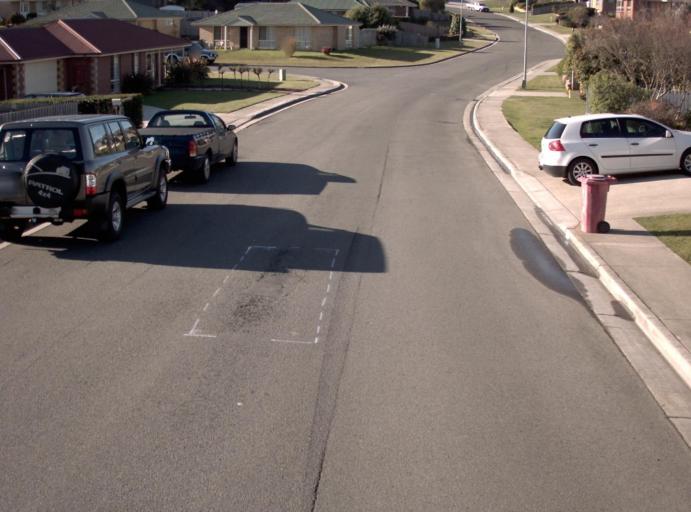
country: AU
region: Tasmania
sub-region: Launceston
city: Summerhill
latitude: -41.4655
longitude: 147.1269
